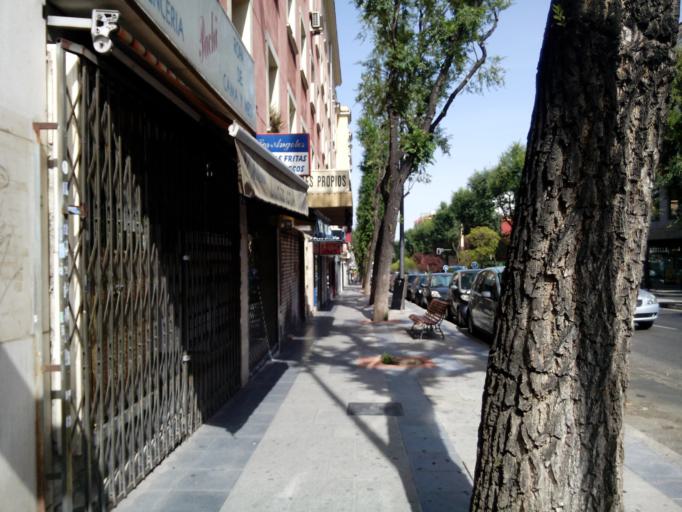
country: ES
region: Madrid
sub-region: Provincia de Madrid
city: Latina
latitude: 40.4099
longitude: -3.7377
